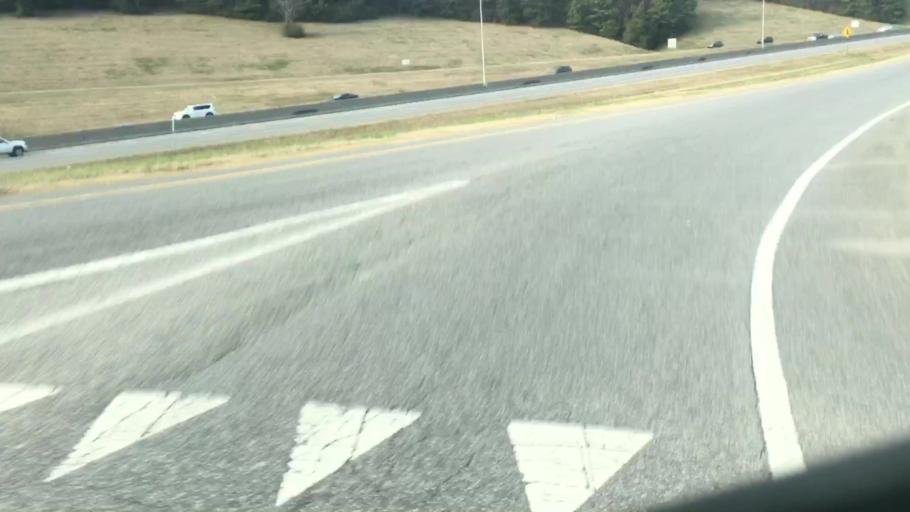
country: US
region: Alabama
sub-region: Jefferson County
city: Cahaba Heights
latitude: 33.4916
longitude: -86.7054
